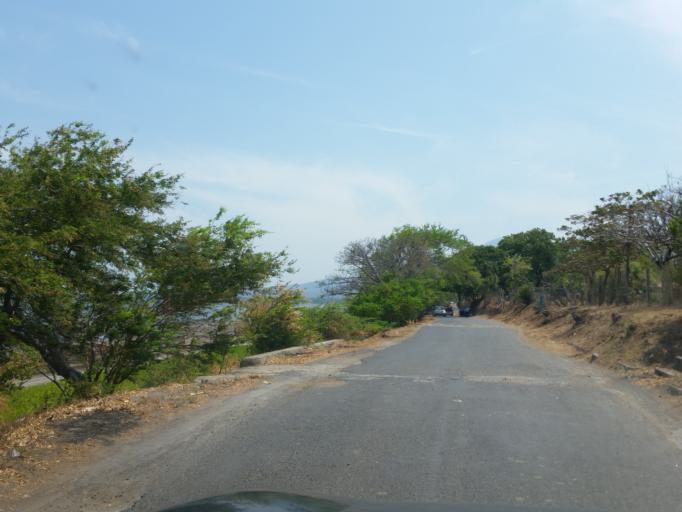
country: NI
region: Granada
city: Granada
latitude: 11.9535
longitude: -85.9456
